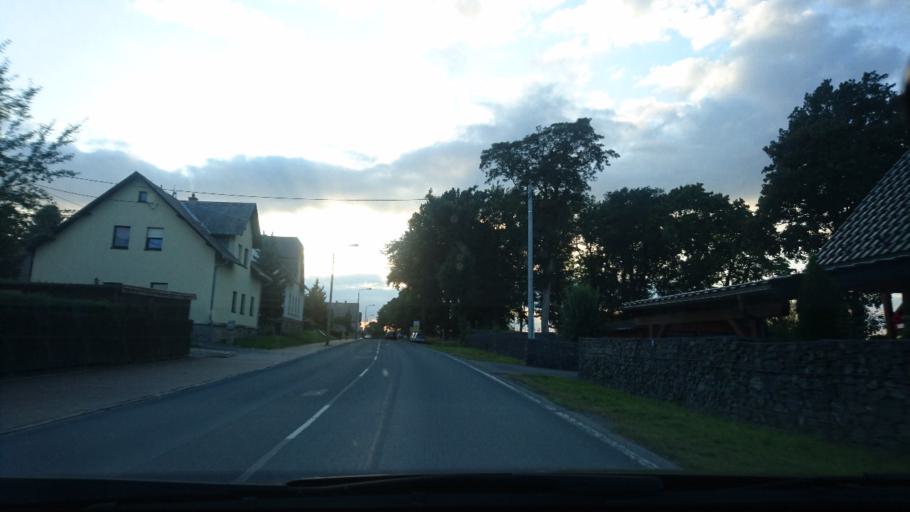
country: DE
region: Saxony
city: Auerbach
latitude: 50.5102
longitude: 12.4196
